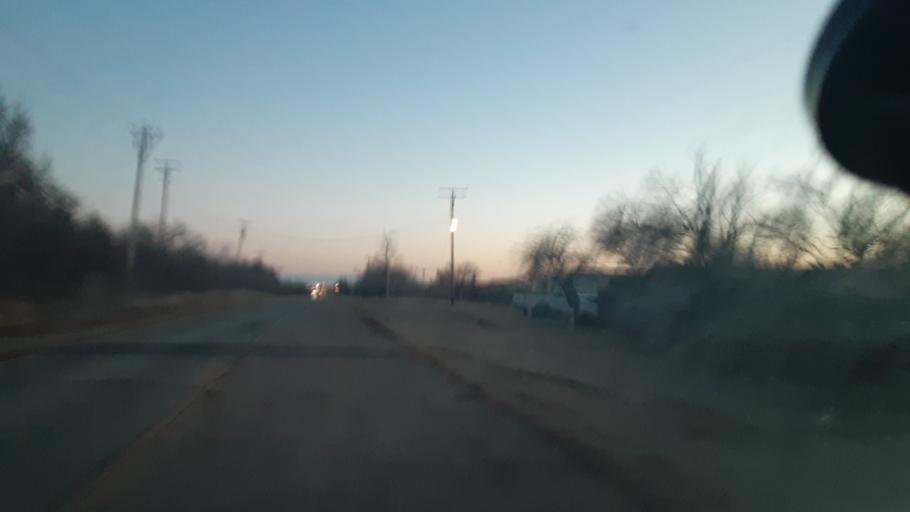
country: US
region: Oklahoma
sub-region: Oklahoma County
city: Edmond
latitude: 35.6592
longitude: -97.4250
